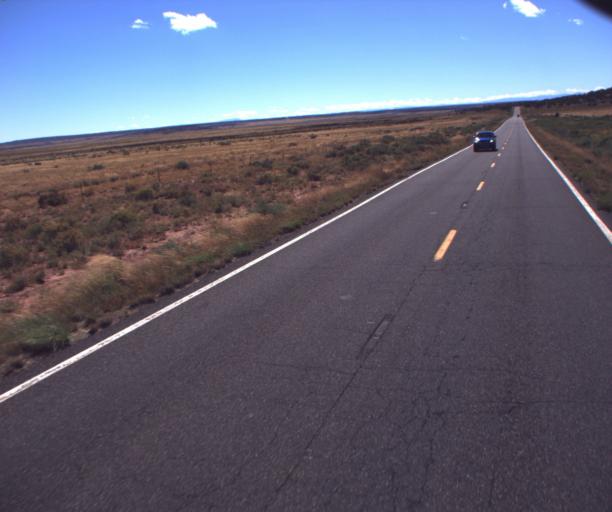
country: US
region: Arizona
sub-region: Apache County
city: Saint Johns
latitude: 34.7466
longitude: -109.2472
